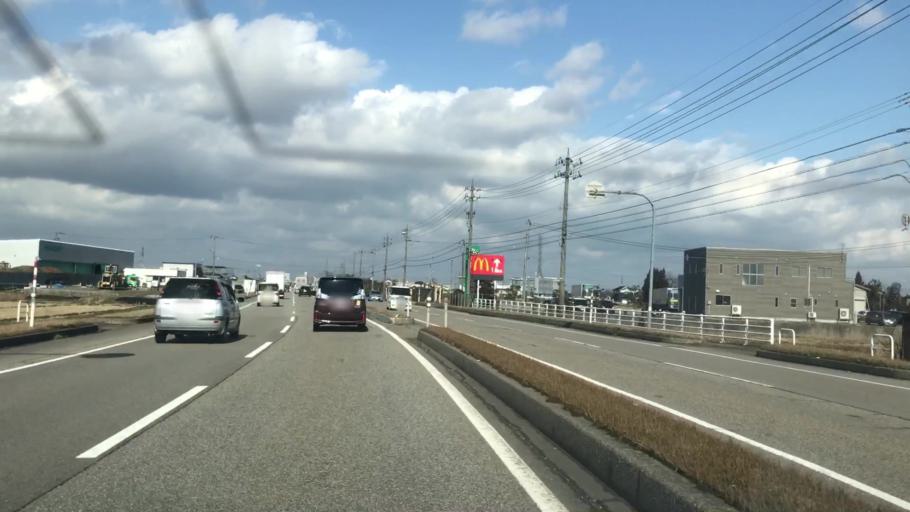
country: JP
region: Toyama
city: Kuragaki-kosugi
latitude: 36.7111
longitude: 137.0806
